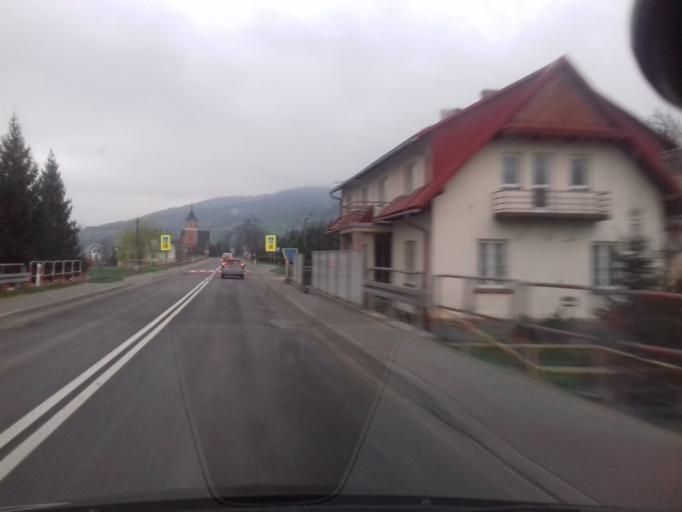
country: PL
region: Lesser Poland Voivodeship
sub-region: Powiat limanowski
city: Mszana Dolna
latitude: 49.7004
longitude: 20.0398
